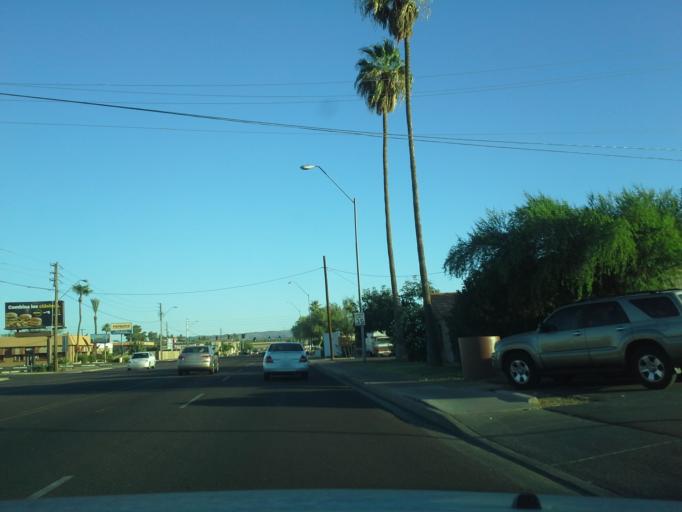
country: US
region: Arizona
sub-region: Maricopa County
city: Phoenix
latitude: 33.4679
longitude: -112.0304
